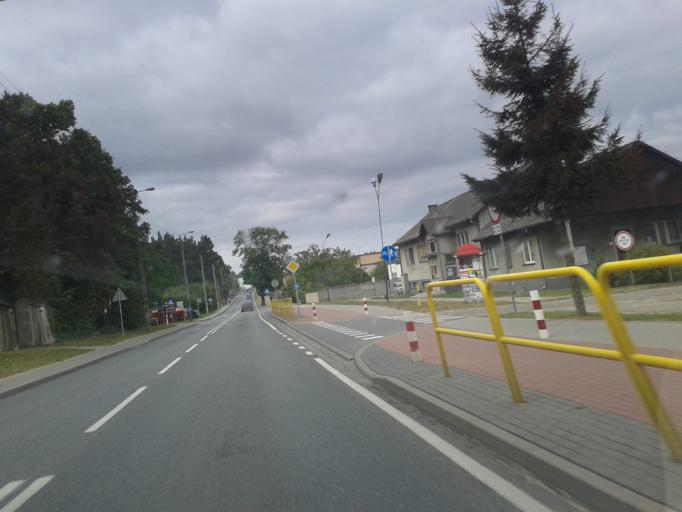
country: PL
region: Kujawsko-Pomorskie
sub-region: Powiat sepolenski
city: Sepolno Krajenskie
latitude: 53.4583
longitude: 17.5329
